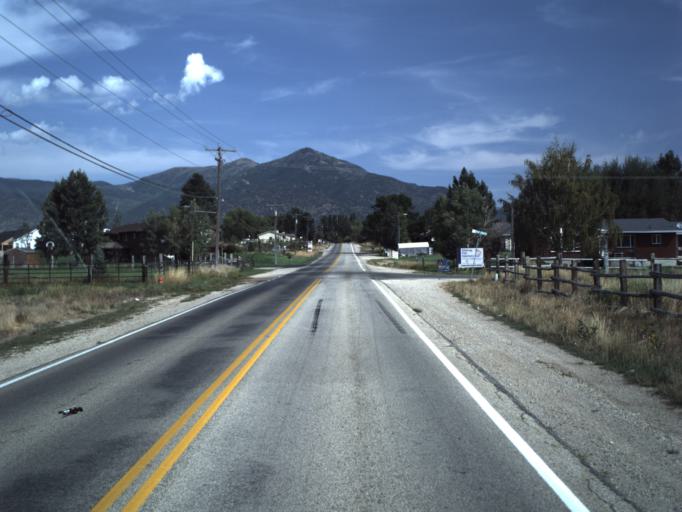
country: US
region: Utah
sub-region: Wasatch County
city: Midway
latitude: 40.4977
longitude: -111.4720
